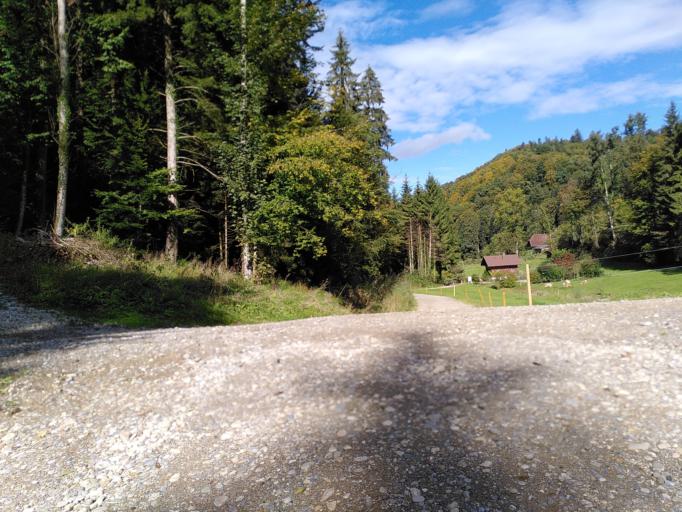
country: CH
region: Bern
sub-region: Oberaargau
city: Seeberg
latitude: 47.1359
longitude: 7.7027
